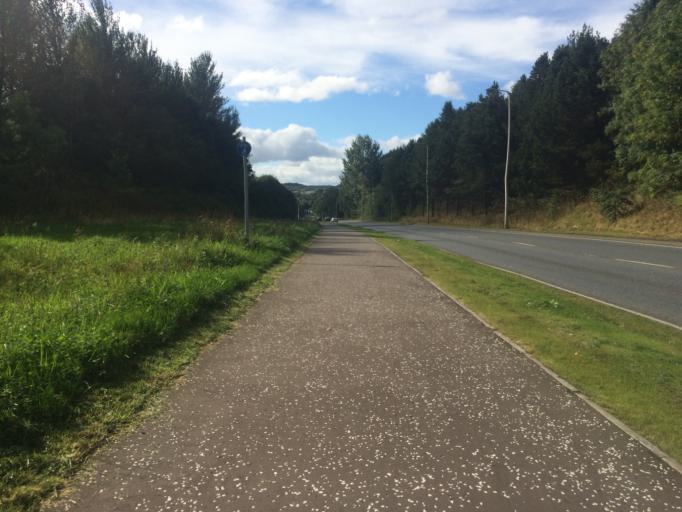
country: GB
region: Scotland
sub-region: Fife
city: Glenrothes
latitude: 56.2086
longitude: -3.1812
